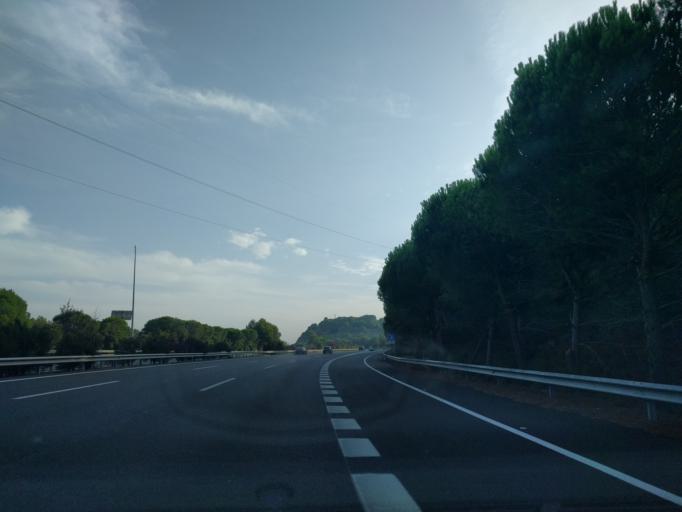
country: ES
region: Catalonia
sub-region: Provincia de Barcelona
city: Pineda de Mar
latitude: 41.6402
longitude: 2.6753
